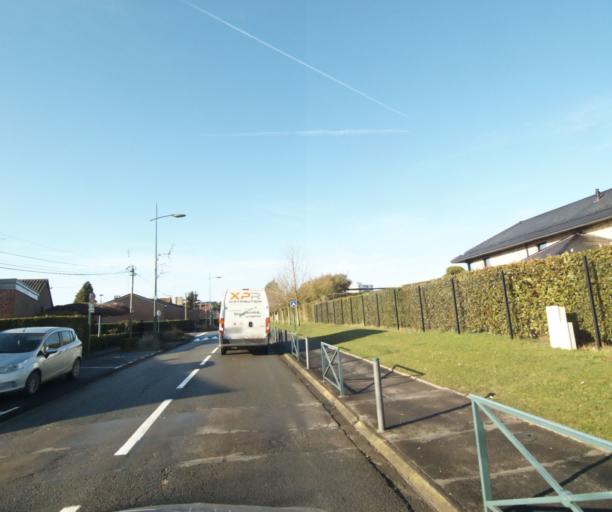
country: FR
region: Nord-Pas-de-Calais
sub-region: Departement du Nord
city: Aulnoy-lez-Valenciennes
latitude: 50.3331
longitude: 3.5266
